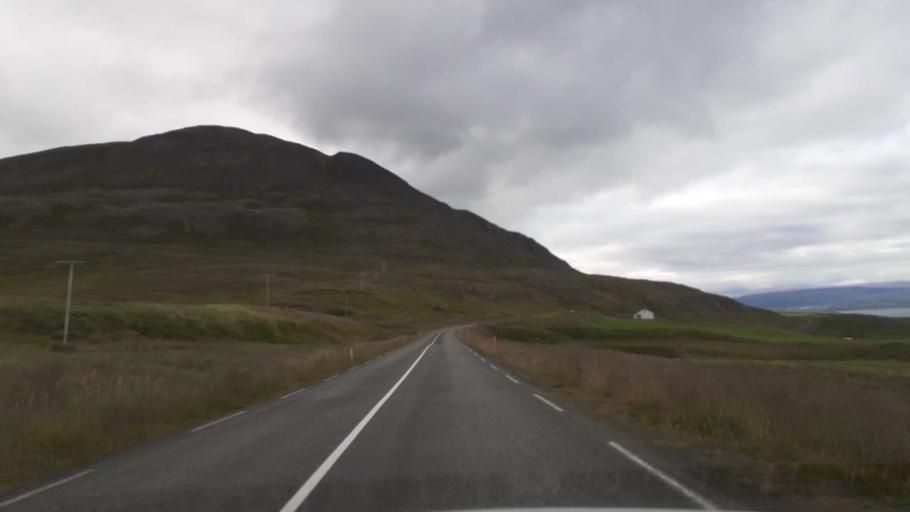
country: IS
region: Northeast
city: Akureyri
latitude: 65.8186
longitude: -18.0494
